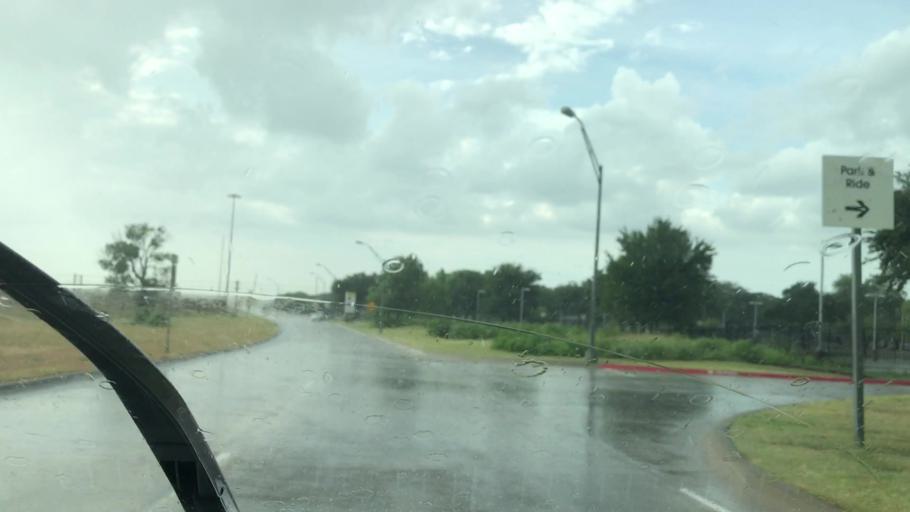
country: US
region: Texas
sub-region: Dallas County
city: Richardson
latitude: 32.8961
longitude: -96.7116
